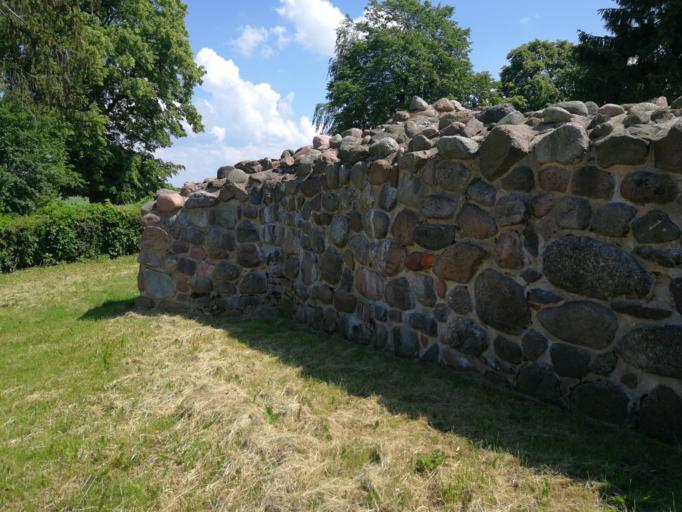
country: PL
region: Warmian-Masurian Voivodeship
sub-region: Powiat ostrodzki
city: Gierzwald
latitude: 53.4836
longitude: 20.1173
